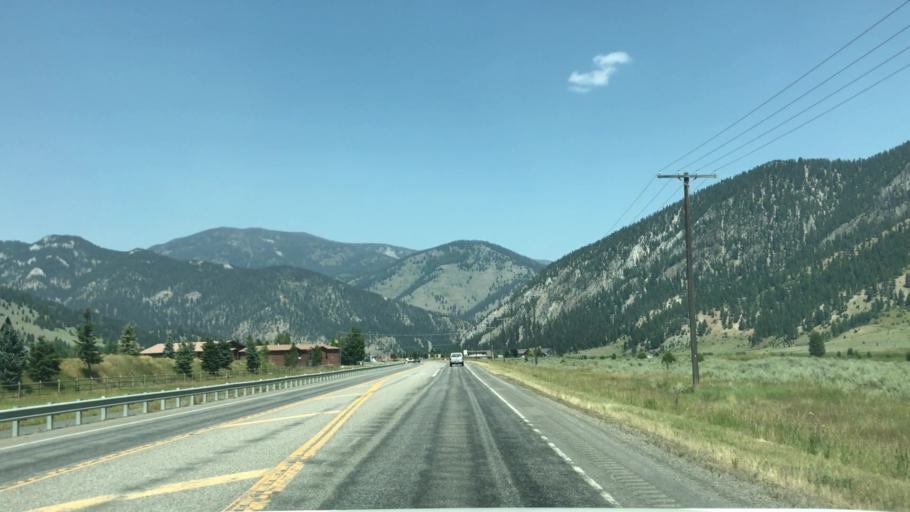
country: US
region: Montana
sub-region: Gallatin County
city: Big Sky
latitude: 45.2423
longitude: -111.2508
